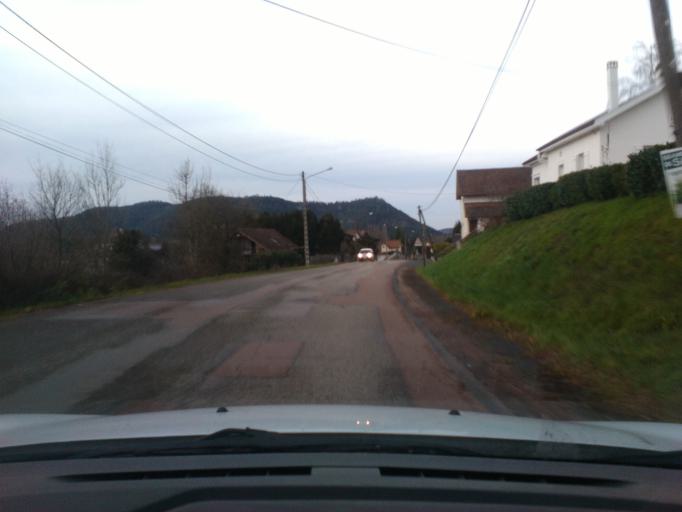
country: FR
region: Lorraine
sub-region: Departement des Vosges
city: Etival-Clairefontaine
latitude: 48.3569
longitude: 6.8800
